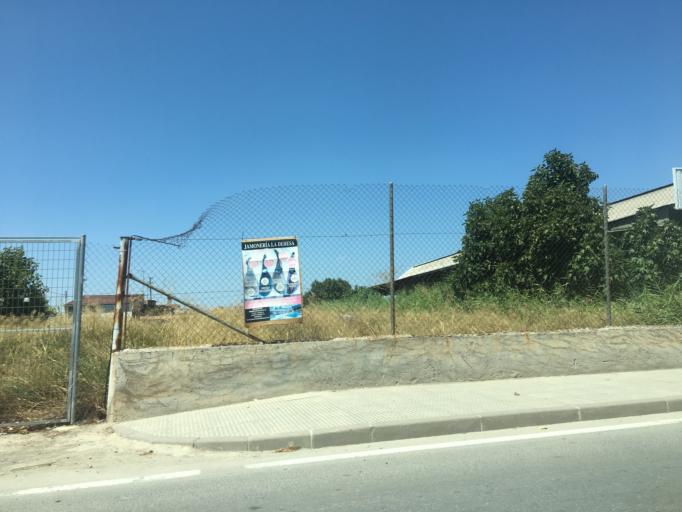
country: ES
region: Murcia
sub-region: Murcia
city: Murcia
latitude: 38.0081
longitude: -1.1139
